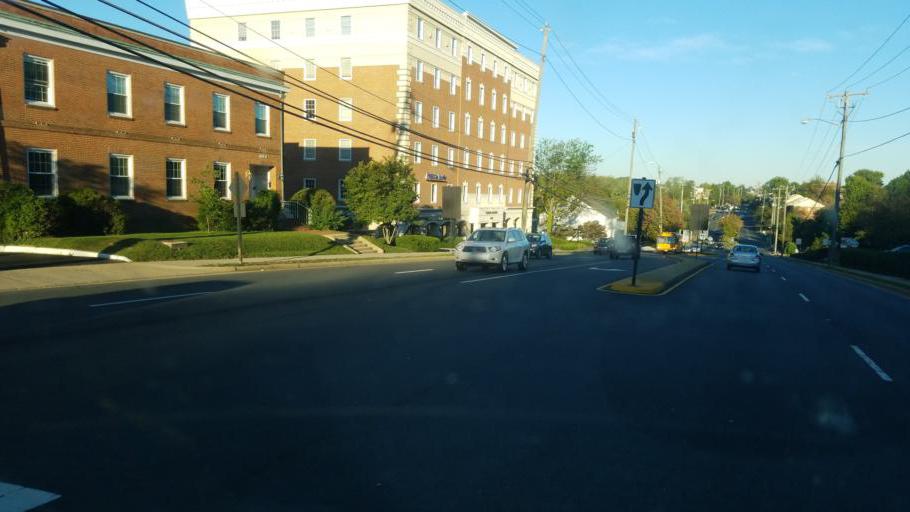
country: US
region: Virginia
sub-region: City of Fairfax
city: Fairfax
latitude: 38.8472
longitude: -77.3096
